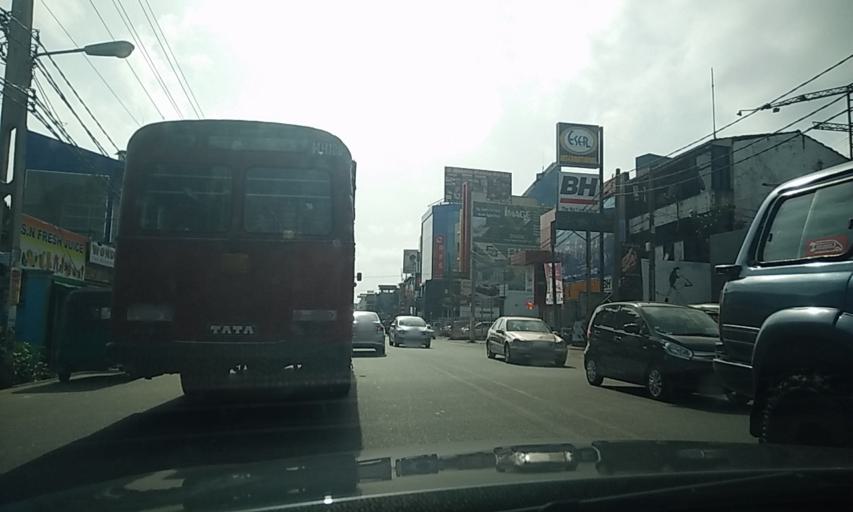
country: LK
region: Western
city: Sri Jayewardenepura Kotte
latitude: 6.8686
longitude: 79.8913
